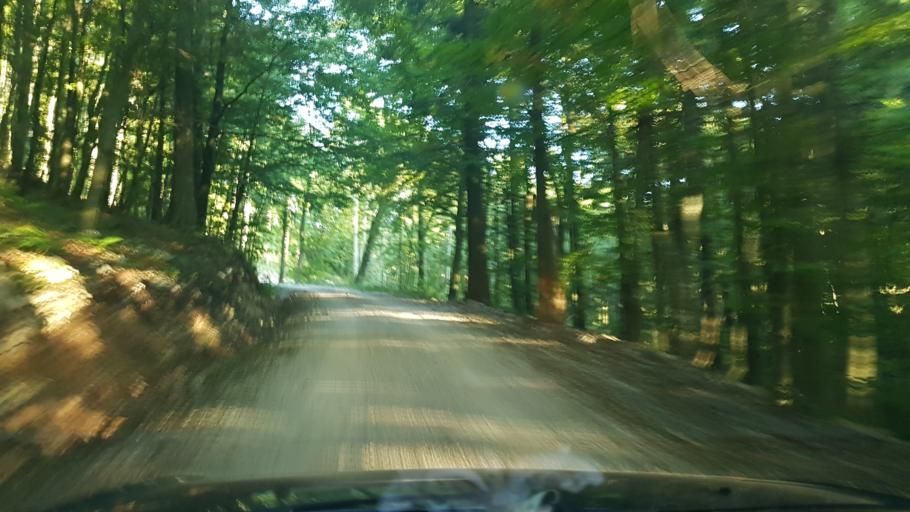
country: SI
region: Vipava
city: Vipava
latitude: 45.7810
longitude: 14.0425
